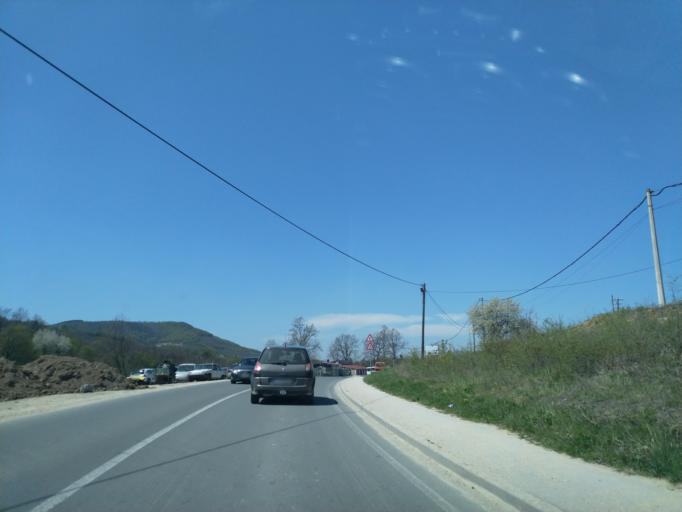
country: RS
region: Central Serbia
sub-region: Sumadijski Okrug
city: Arangelovac
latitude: 44.3261
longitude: 20.5257
